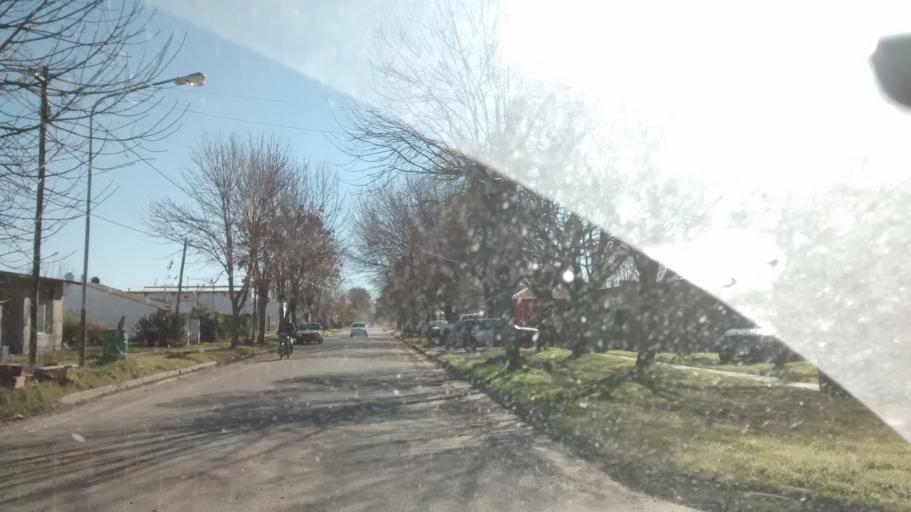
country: AR
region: Buenos Aires
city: Pila
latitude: -36.0007
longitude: -58.1423
